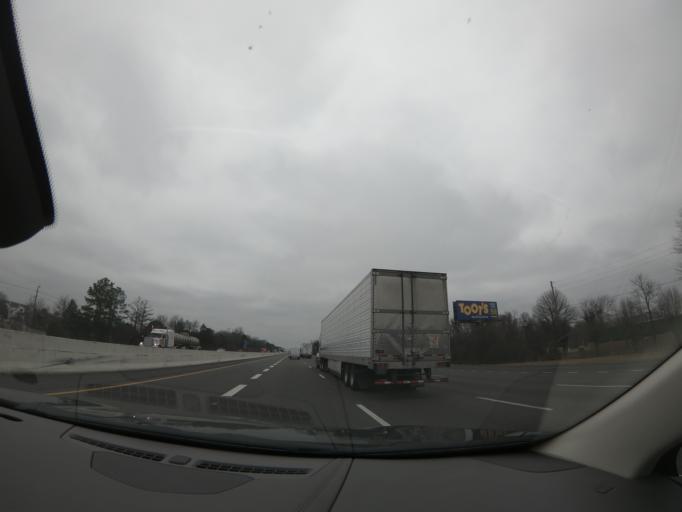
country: US
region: Tennessee
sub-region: Rutherford County
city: Murfreesboro
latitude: 35.8516
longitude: -86.4398
